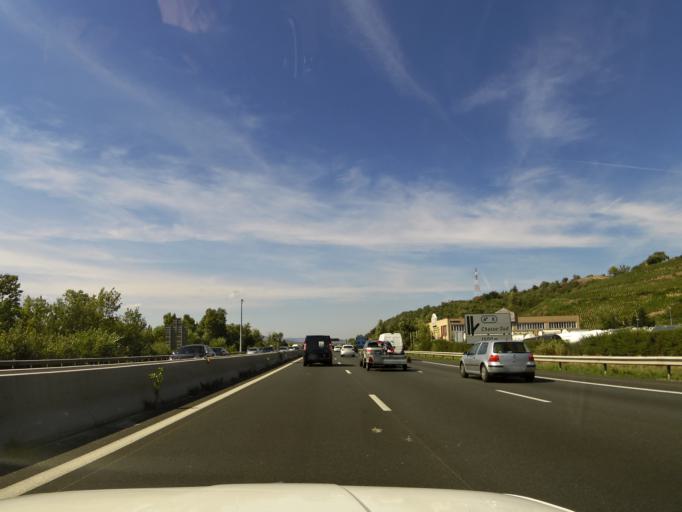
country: FR
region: Rhone-Alpes
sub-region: Departement du Rhone
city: Loire-sur-Rhone
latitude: 45.5570
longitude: 4.8244
